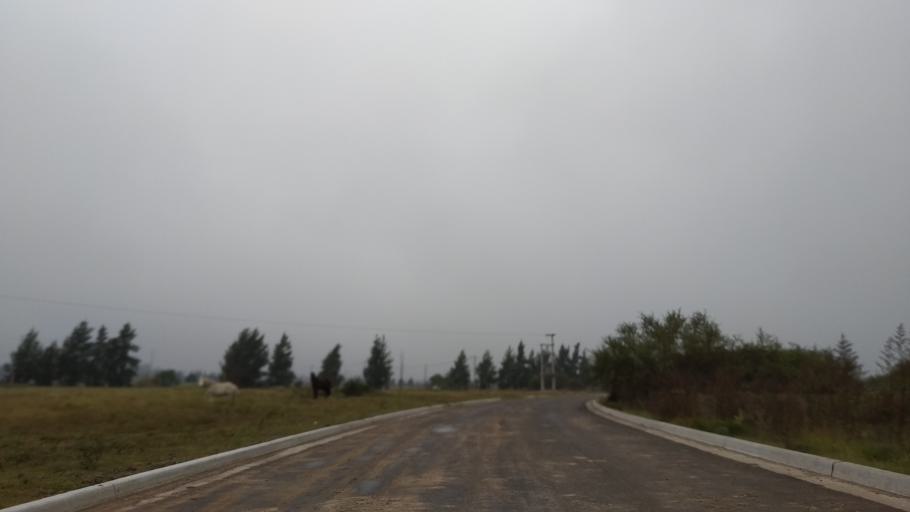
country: AR
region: Santa Fe
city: Funes
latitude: -32.9360
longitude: -60.7678
